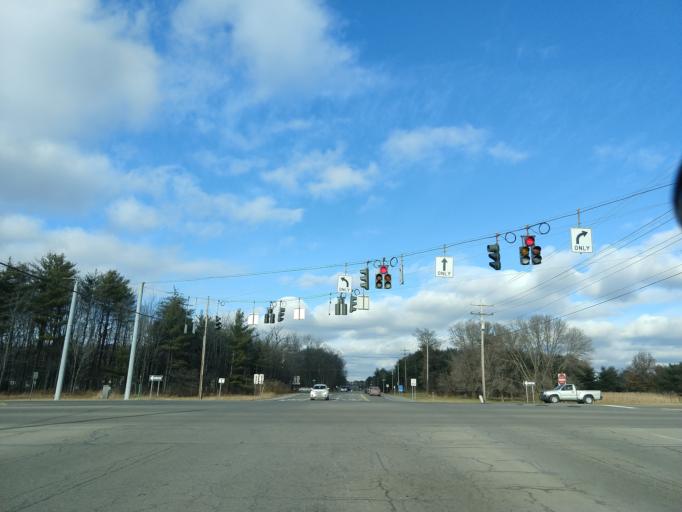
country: US
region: New York
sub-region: Tompkins County
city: Northeast Ithaca
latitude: 42.4821
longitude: -76.4673
